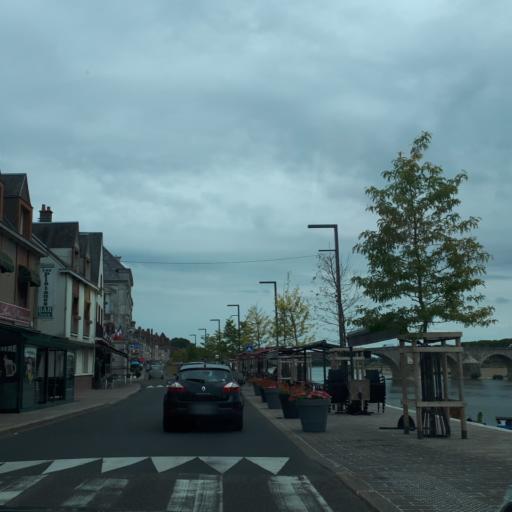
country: FR
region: Centre
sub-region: Departement du Loiret
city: Gien
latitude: 47.6847
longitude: 2.6284
